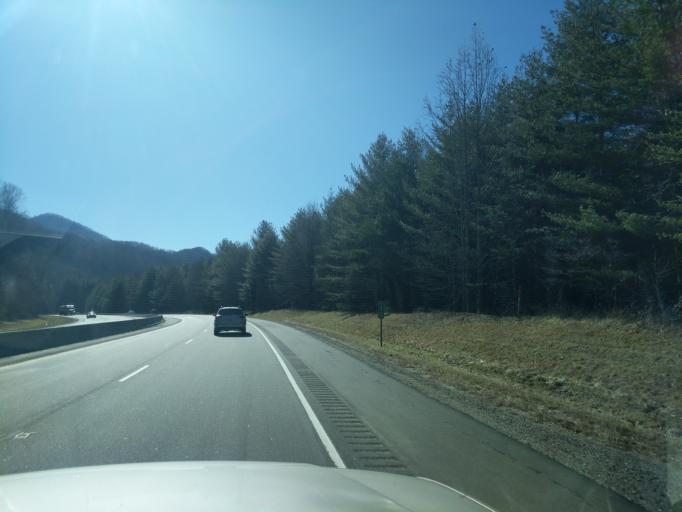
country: US
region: North Carolina
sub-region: Jackson County
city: Cullowhee
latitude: 35.4046
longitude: -83.1247
